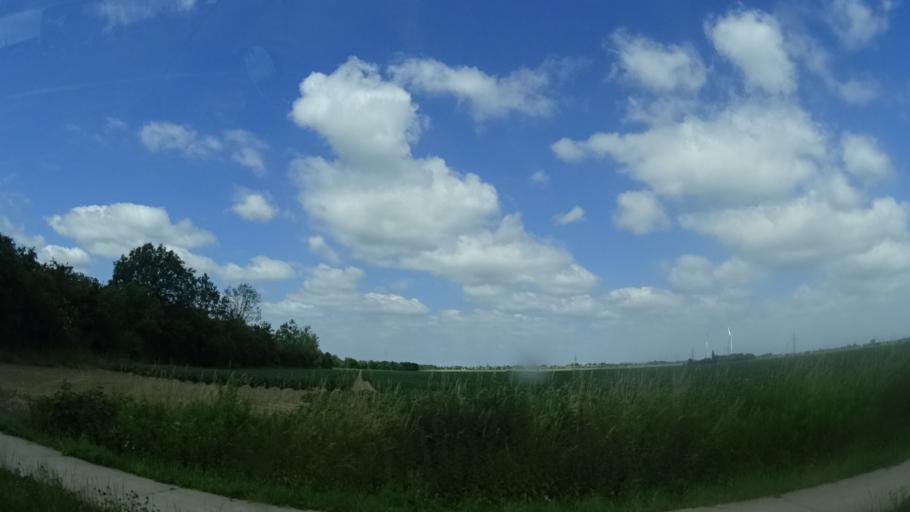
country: DE
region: Lower Saxony
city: Hildesheim
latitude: 52.1615
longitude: 9.9989
